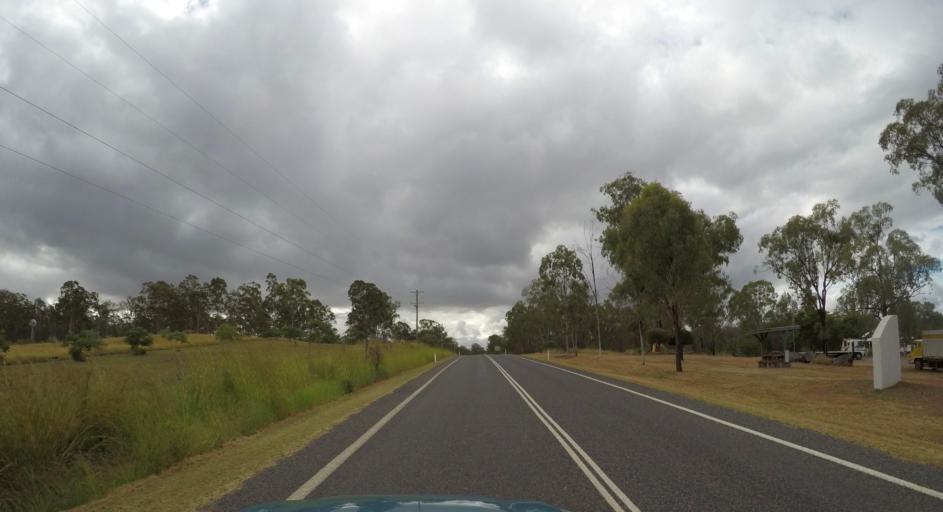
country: AU
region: Queensland
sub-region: North Burnett
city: Gayndah
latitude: -25.3623
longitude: 151.1197
